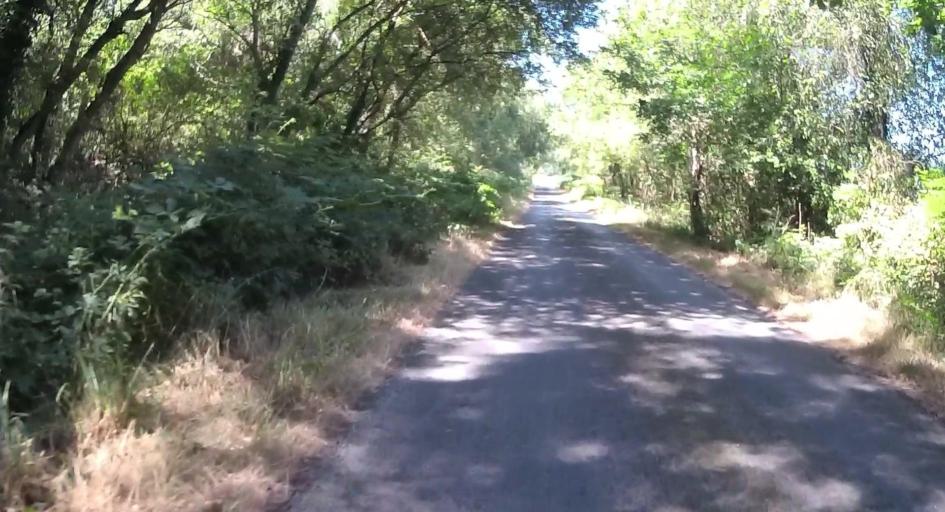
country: GB
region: England
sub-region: Dorset
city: Bovington Camp
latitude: 50.6877
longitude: -2.2973
